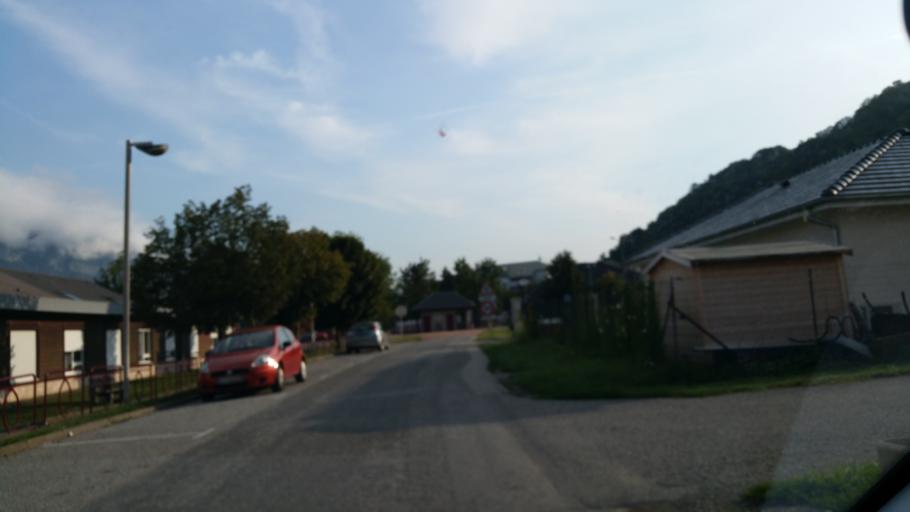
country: FR
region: Rhone-Alpes
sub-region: Departement de la Savoie
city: Aiton
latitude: 45.5622
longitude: 6.2494
